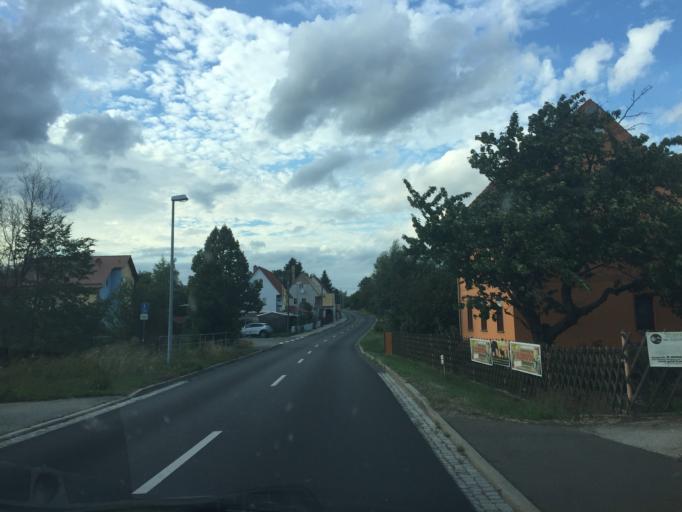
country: DE
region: Thuringia
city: Schmolln
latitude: 50.9099
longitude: 12.3510
